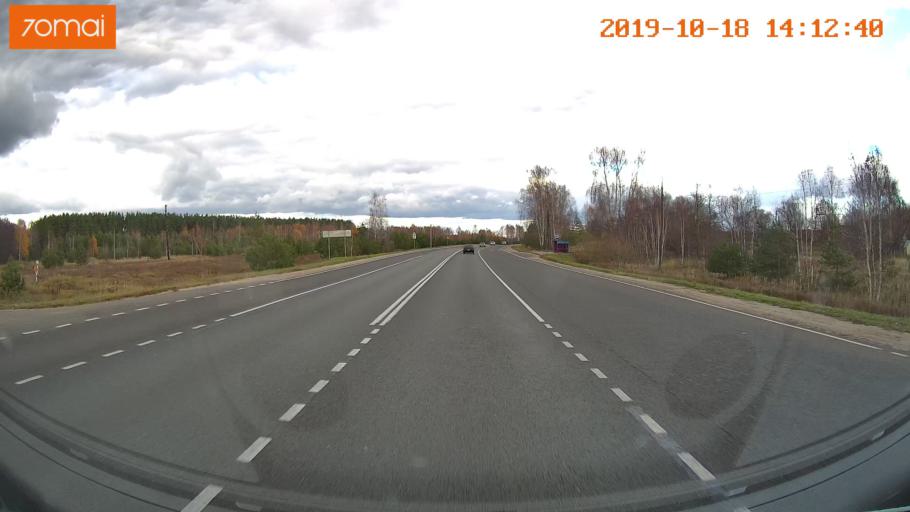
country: RU
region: Rjazan
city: Spas-Klepiki
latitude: 55.1480
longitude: 40.2546
